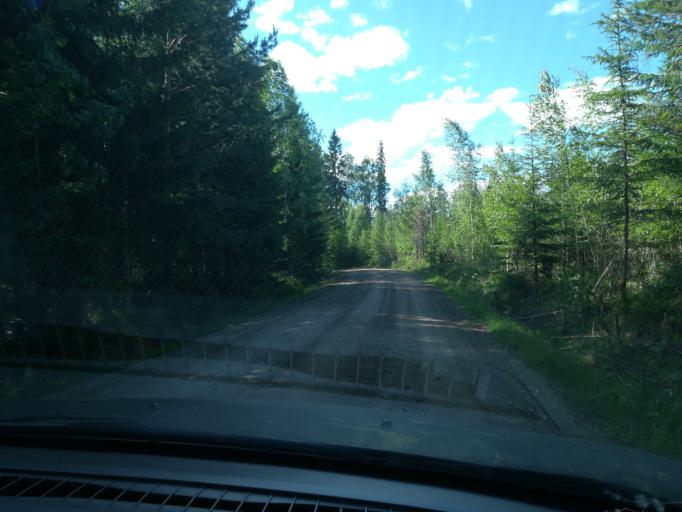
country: FI
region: Southern Savonia
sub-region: Mikkeli
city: Puumala
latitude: 61.6544
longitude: 28.1695
